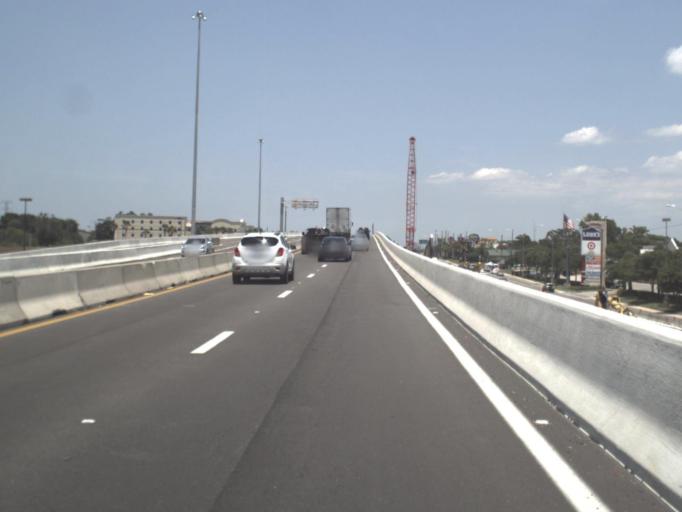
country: US
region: Florida
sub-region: Pinellas County
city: South Highpoint
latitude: 27.9573
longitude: -82.7301
